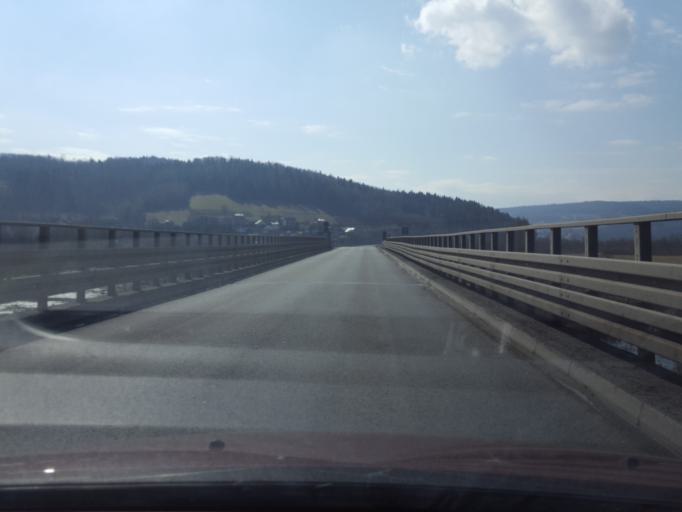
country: PL
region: Lesser Poland Voivodeship
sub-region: Powiat nowosadecki
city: Chelmiec
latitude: 49.6888
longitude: 20.6548
